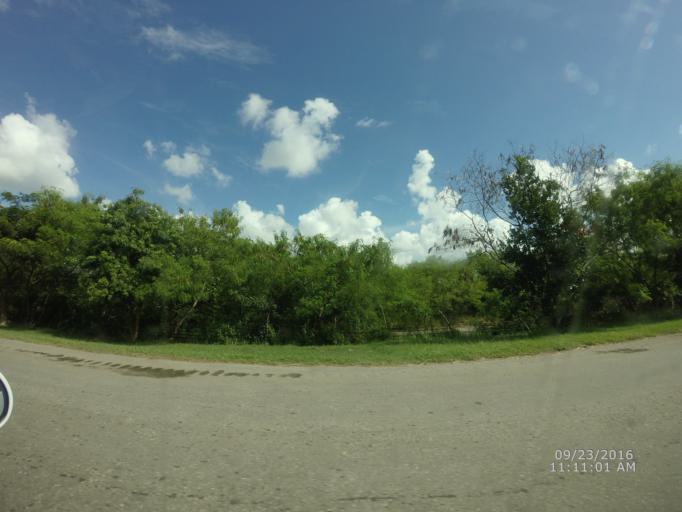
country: CU
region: La Habana
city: Arroyo Naranjo
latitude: 23.0237
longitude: -82.2637
